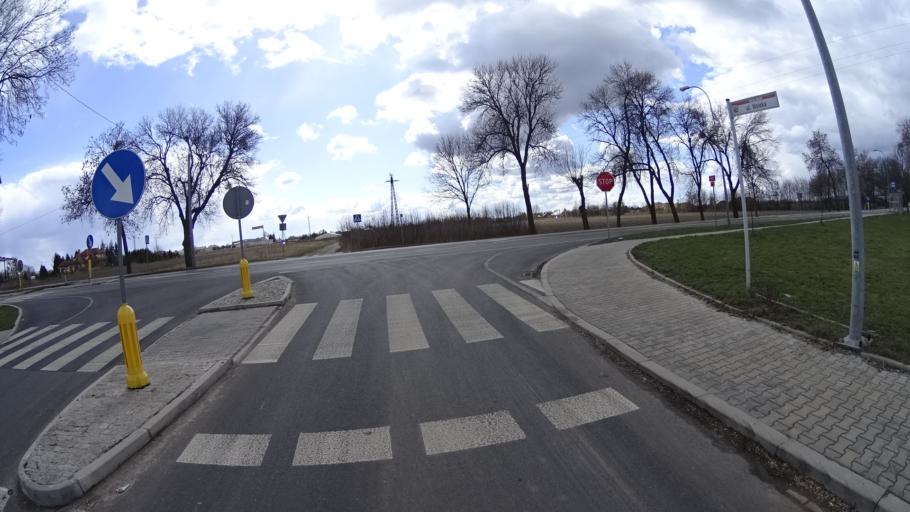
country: PL
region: Masovian Voivodeship
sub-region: Powiat warszawski zachodni
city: Jozefow
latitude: 52.2126
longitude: 20.7149
